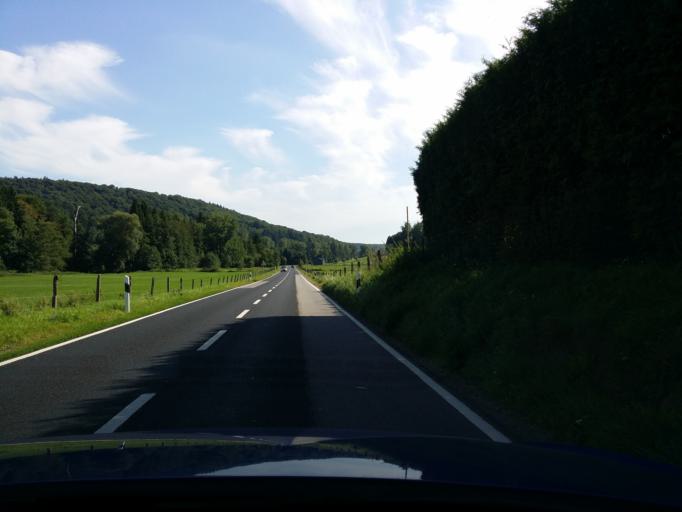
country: LU
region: Luxembourg
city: Rollingen
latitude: 49.7163
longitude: 6.0901
